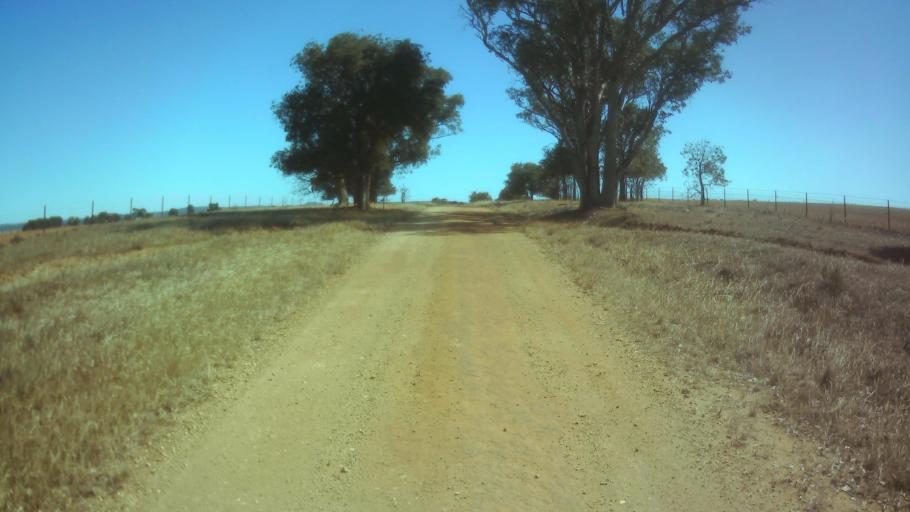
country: AU
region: New South Wales
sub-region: Weddin
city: Grenfell
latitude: -33.9769
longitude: 148.3426
